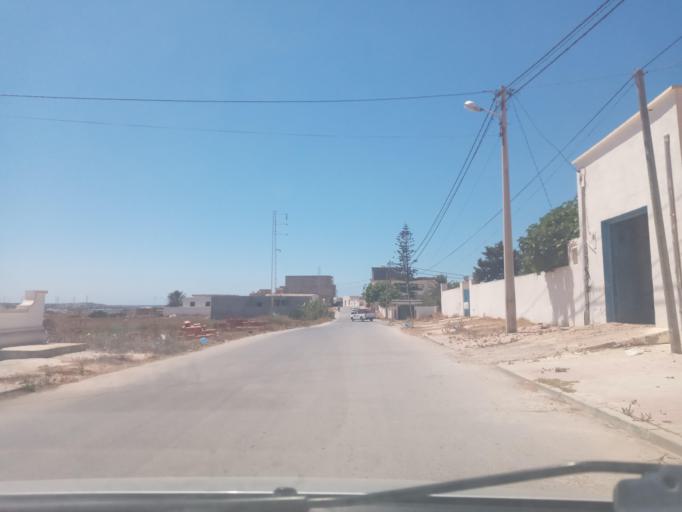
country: TN
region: Nabul
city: El Haouaria
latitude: 37.0536
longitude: 10.9945
